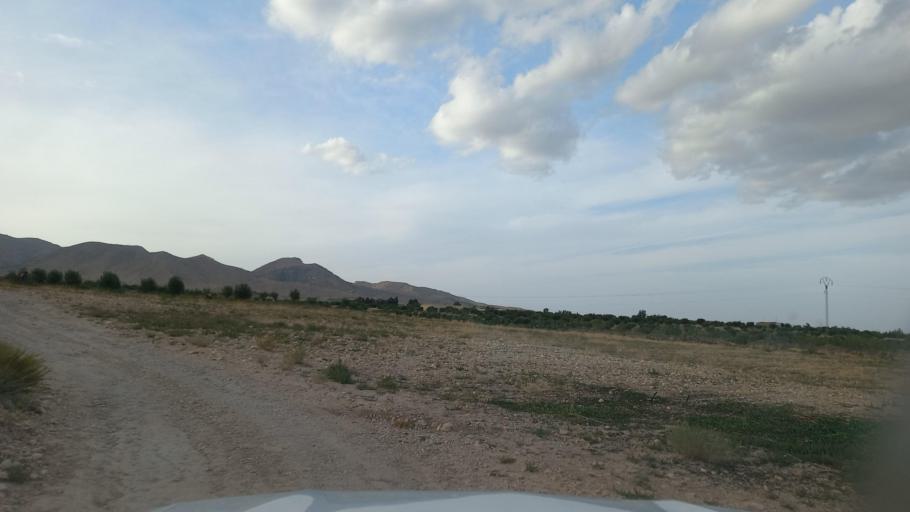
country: TN
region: Al Qasrayn
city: Sbiba
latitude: 35.4358
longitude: 9.0981
